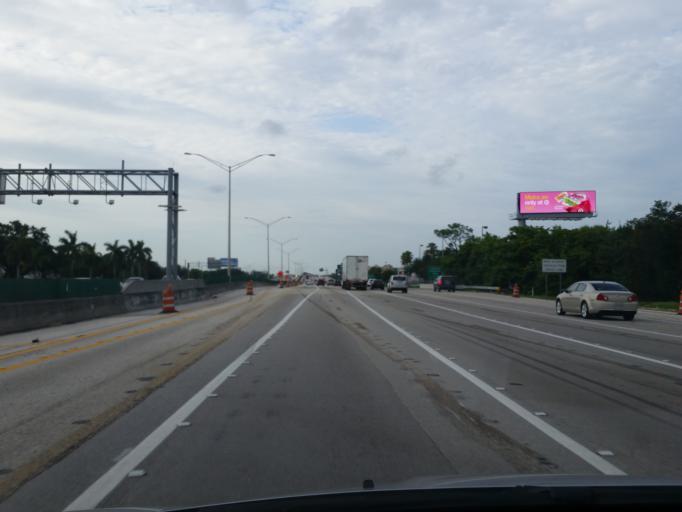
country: US
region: Florida
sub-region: Broward County
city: Dania Beach
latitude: 26.0397
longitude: -80.1633
